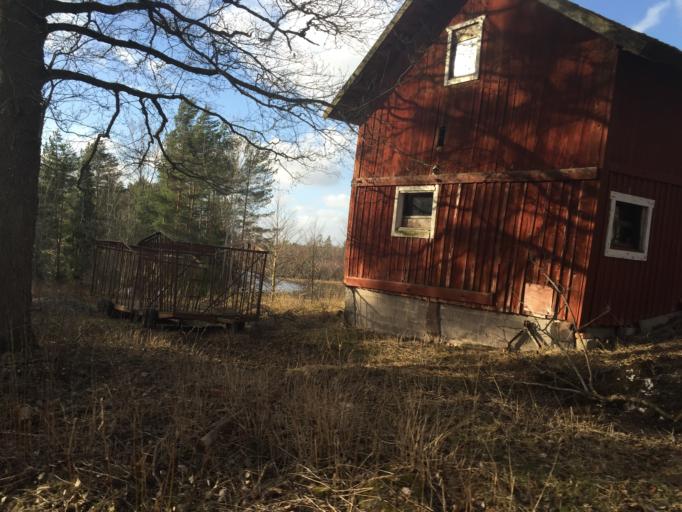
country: SE
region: Soedermanland
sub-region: Vingakers Kommun
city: Vingaker
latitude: 58.9879
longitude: 15.7325
